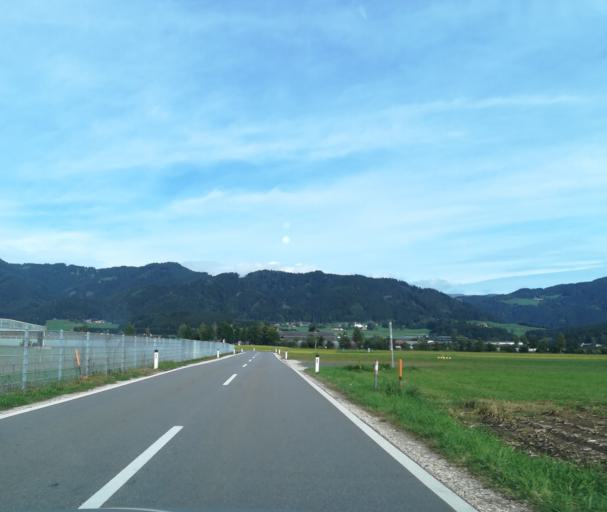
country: AT
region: Styria
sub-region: Politischer Bezirk Murtal
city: Flatschach
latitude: 47.2037
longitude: 14.7609
